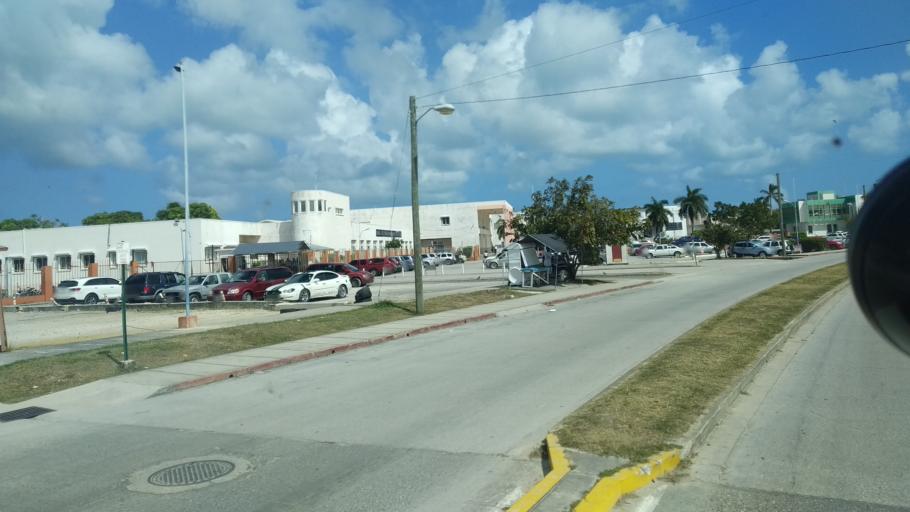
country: BZ
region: Belize
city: Belize City
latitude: 17.5076
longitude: -88.1970
